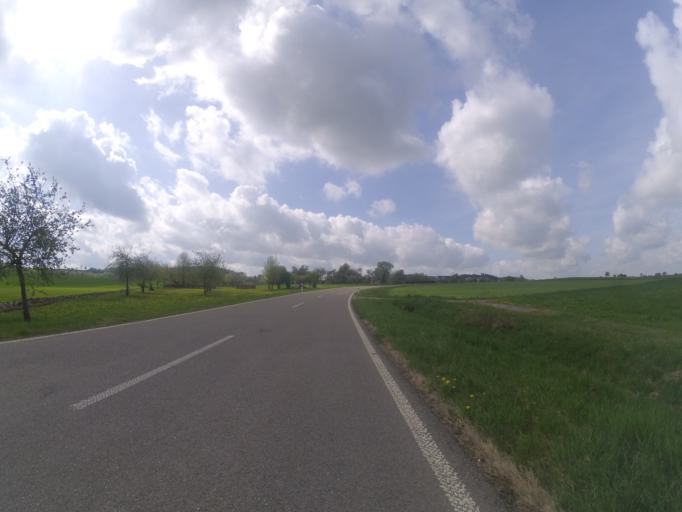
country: DE
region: Baden-Wuerttemberg
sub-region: Tuebingen Region
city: Griesingen
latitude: 48.2359
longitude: 9.7687
